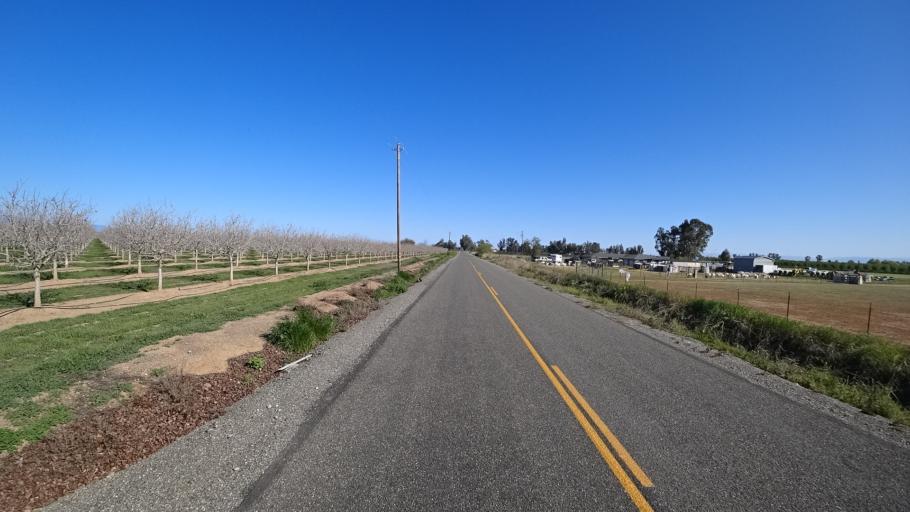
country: US
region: California
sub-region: Glenn County
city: Orland
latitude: 39.7487
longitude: -122.2481
